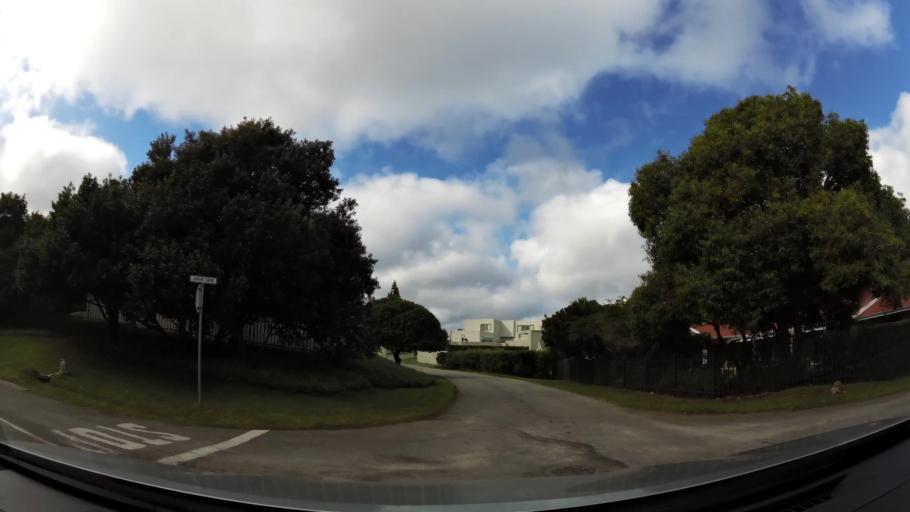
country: ZA
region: Western Cape
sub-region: Eden District Municipality
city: Plettenberg Bay
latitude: -34.0725
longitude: 23.3708
